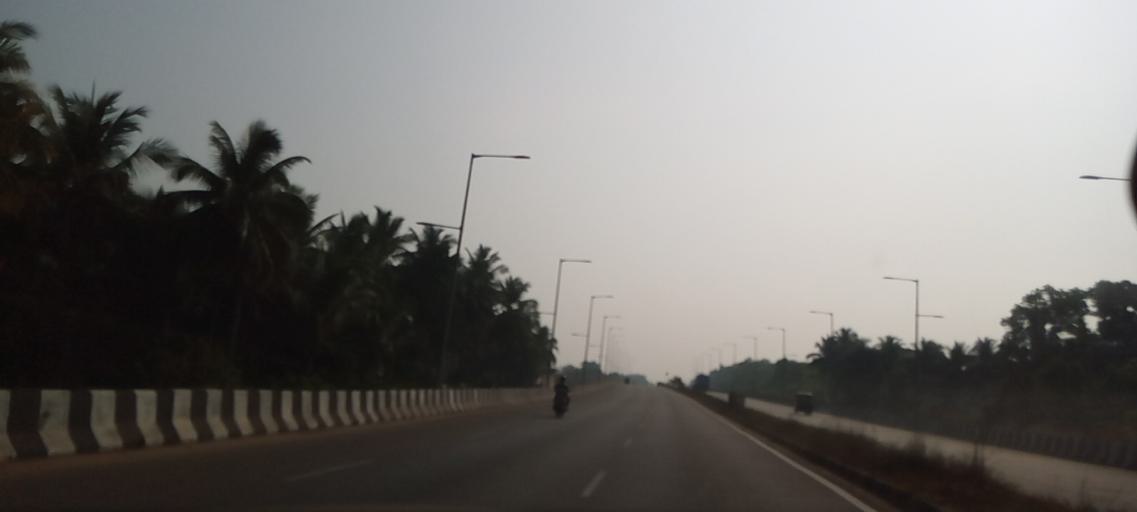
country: IN
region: Karnataka
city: Gangolli
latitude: 13.6881
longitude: 74.6579
